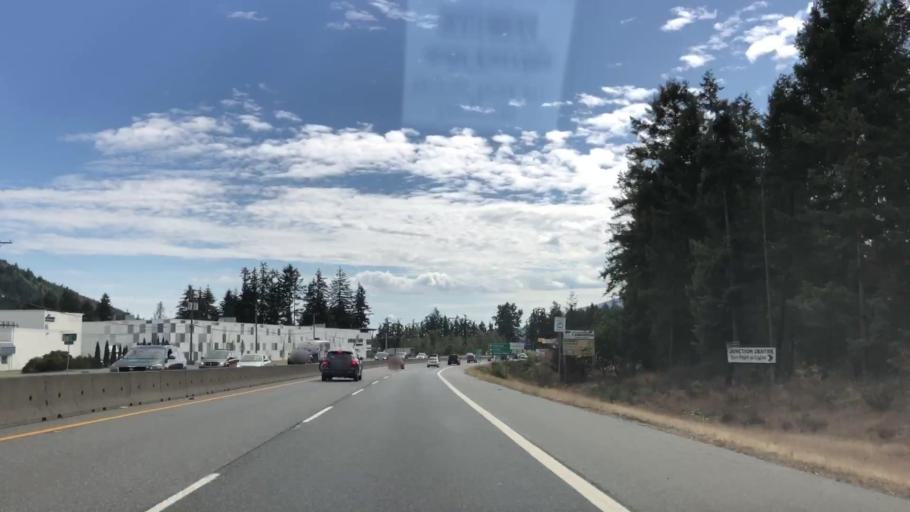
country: CA
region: British Columbia
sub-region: Cowichan Valley Regional District
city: Ladysmith
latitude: 49.0384
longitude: -123.8654
